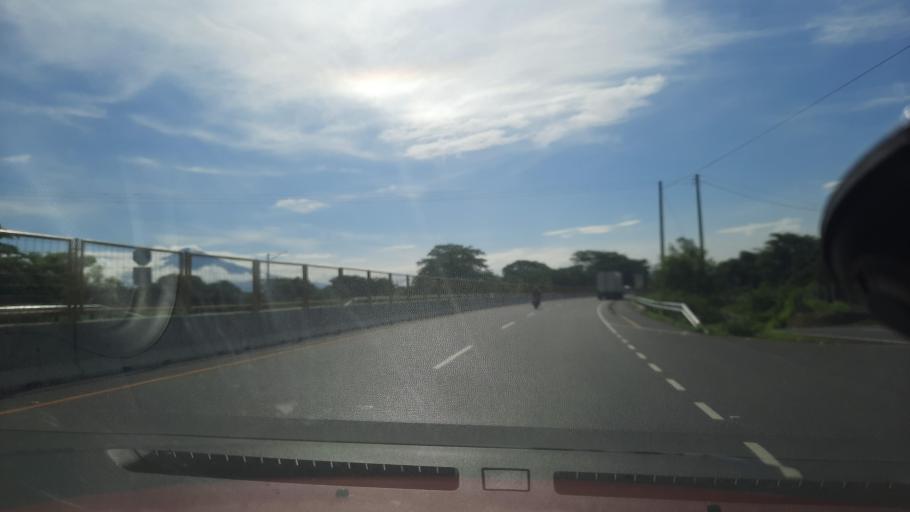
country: SV
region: La Paz
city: El Rosario
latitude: 13.4861
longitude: -88.9936
